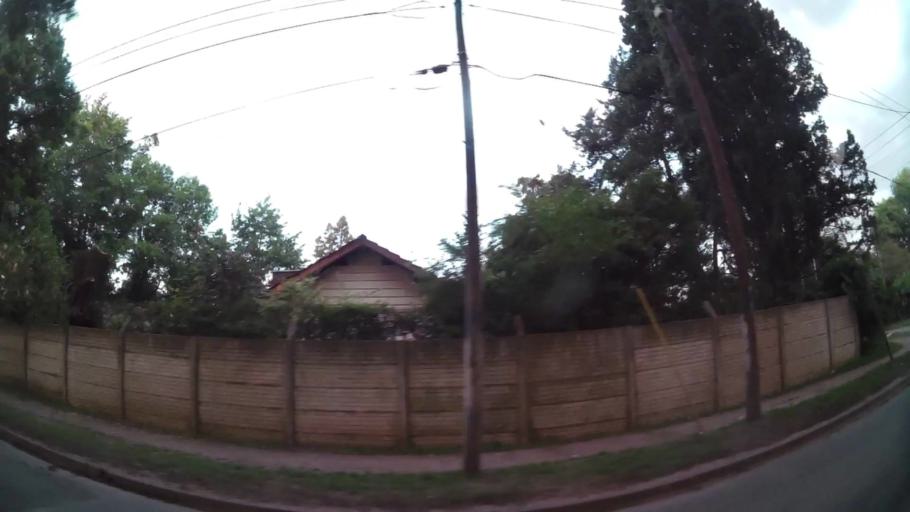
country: AR
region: Buenos Aires
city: Santa Catalina - Dique Lujan
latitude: -34.4800
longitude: -58.7820
